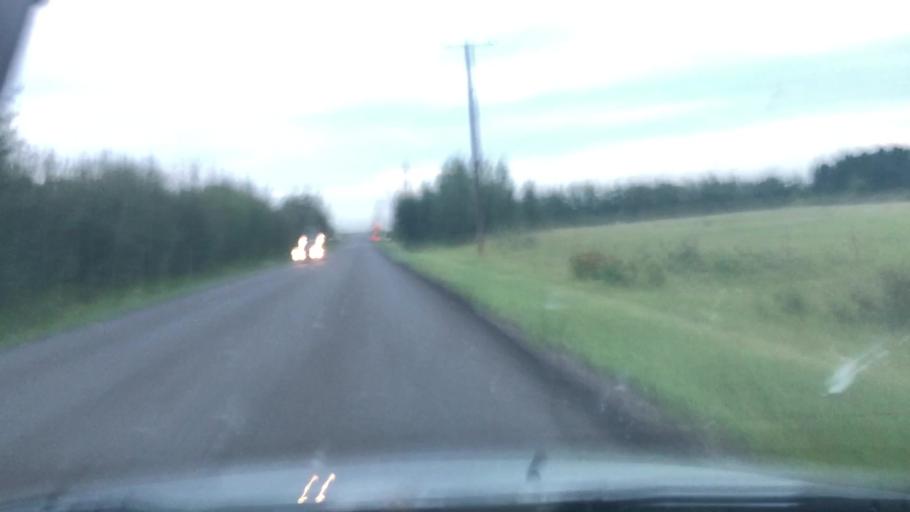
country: CA
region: Alberta
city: Devon
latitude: 53.4807
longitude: -113.6890
